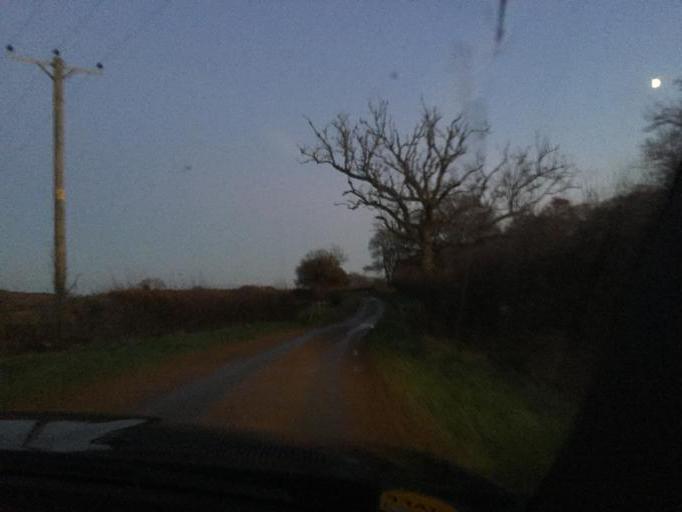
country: GB
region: England
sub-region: Northamptonshire
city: Silverstone
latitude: 52.0869
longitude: -1.0850
